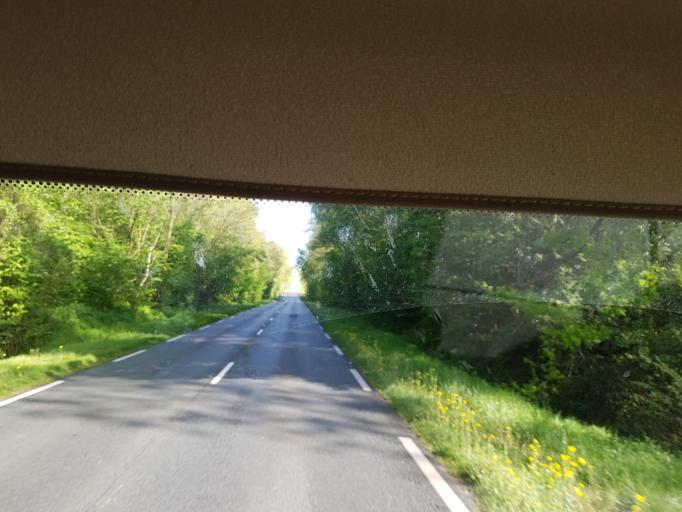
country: FR
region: Picardie
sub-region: Departement de l'Aisne
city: Sinceny
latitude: 49.6081
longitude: 3.2707
